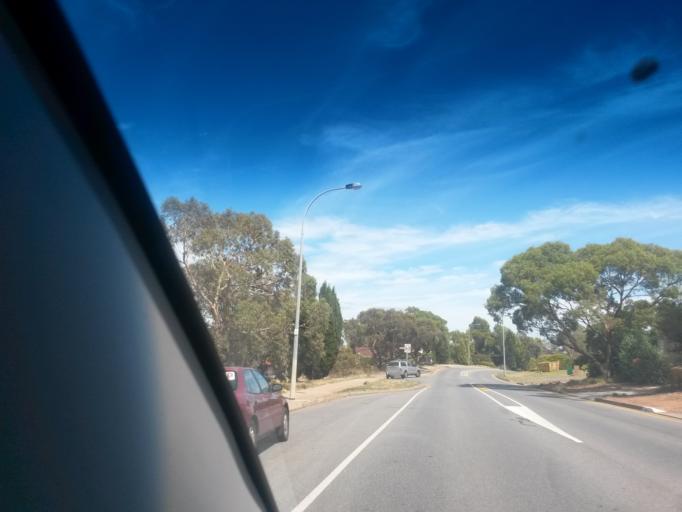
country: AU
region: South Australia
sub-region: Tea Tree Gully
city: Golden Grove
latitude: -34.7673
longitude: 138.6980
